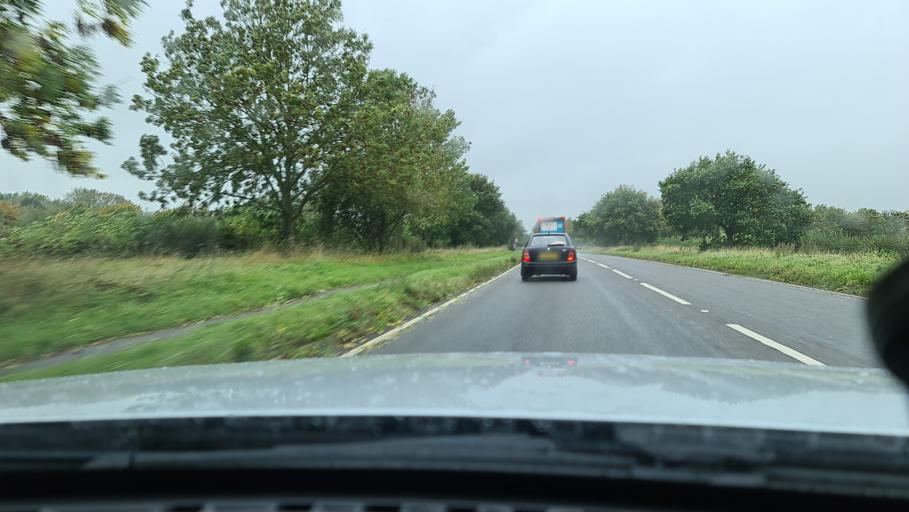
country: GB
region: England
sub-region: Oxfordshire
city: Deddington
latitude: 51.9867
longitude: -1.3221
